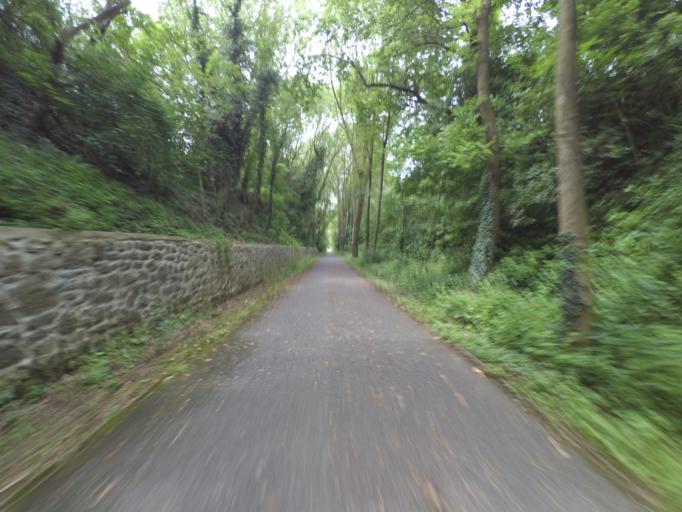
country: DE
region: North Rhine-Westphalia
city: Stolberg
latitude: 50.7261
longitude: 6.1830
